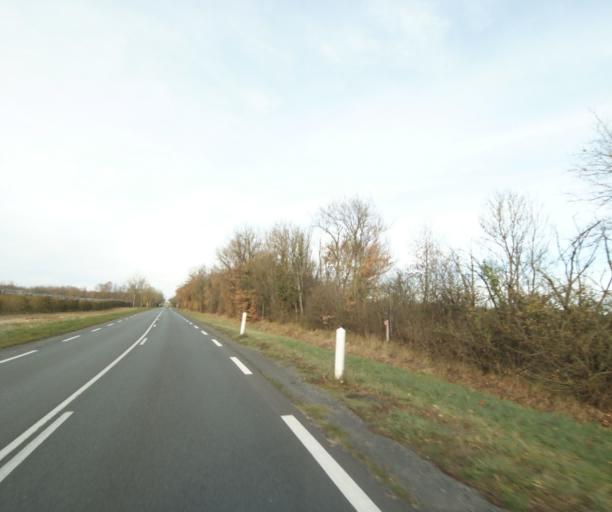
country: FR
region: Poitou-Charentes
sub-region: Departement de la Charente-Maritime
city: Fontcouverte
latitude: 45.7785
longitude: -0.5712
